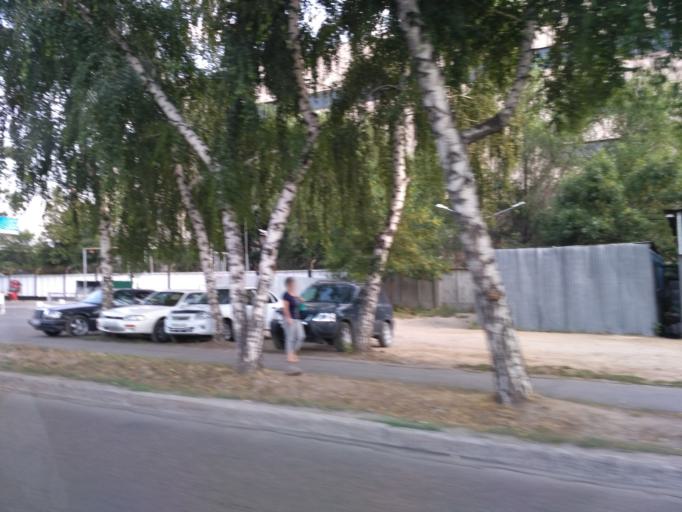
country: KZ
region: Almaty Qalasy
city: Almaty
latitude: 43.2415
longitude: 76.8408
